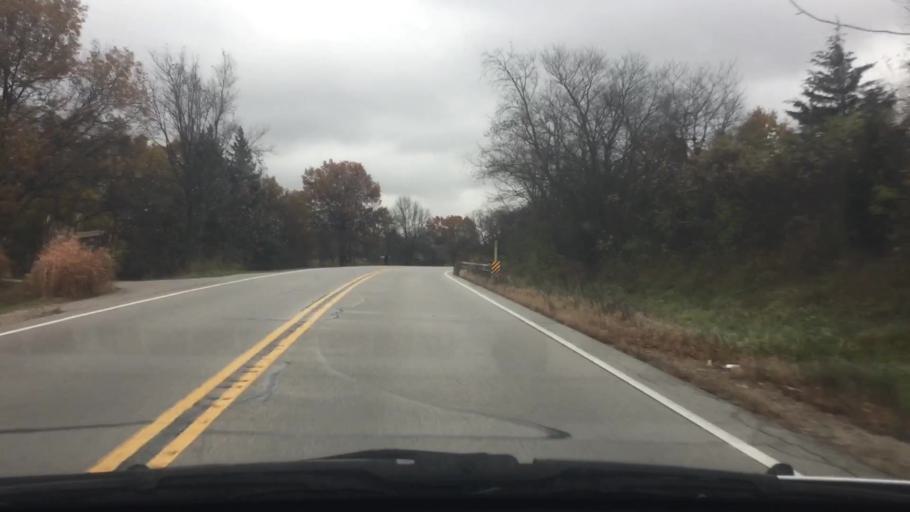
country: US
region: Wisconsin
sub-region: Waukesha County
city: Eagle
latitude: 42.8975
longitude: -88.4738
